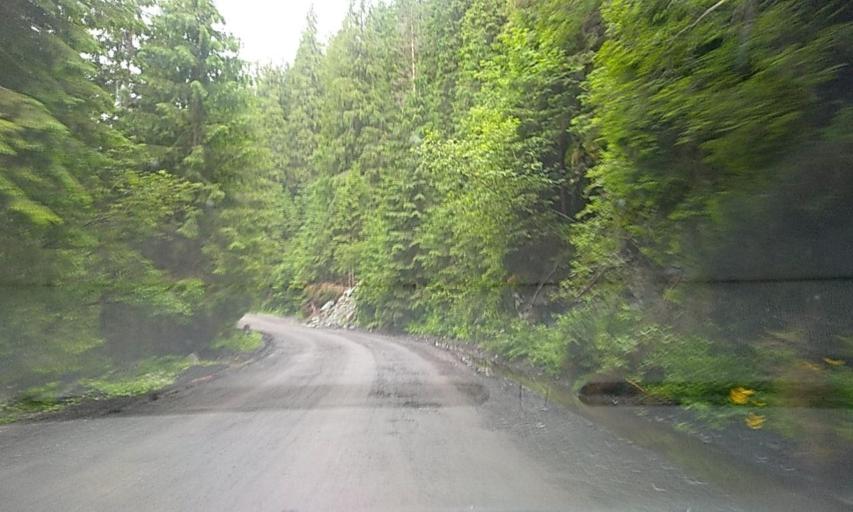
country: RO
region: Hunedoara
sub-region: Oras Petrila
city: Petrila
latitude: 45.4087
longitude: 23.5356
